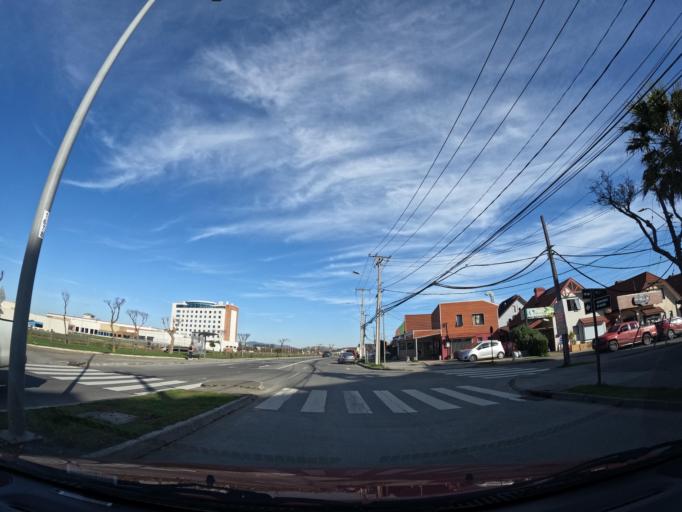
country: CL
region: Biobio
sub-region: Provincia de Concepcion
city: Concepcion
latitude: -36.7749
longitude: -73.0757
